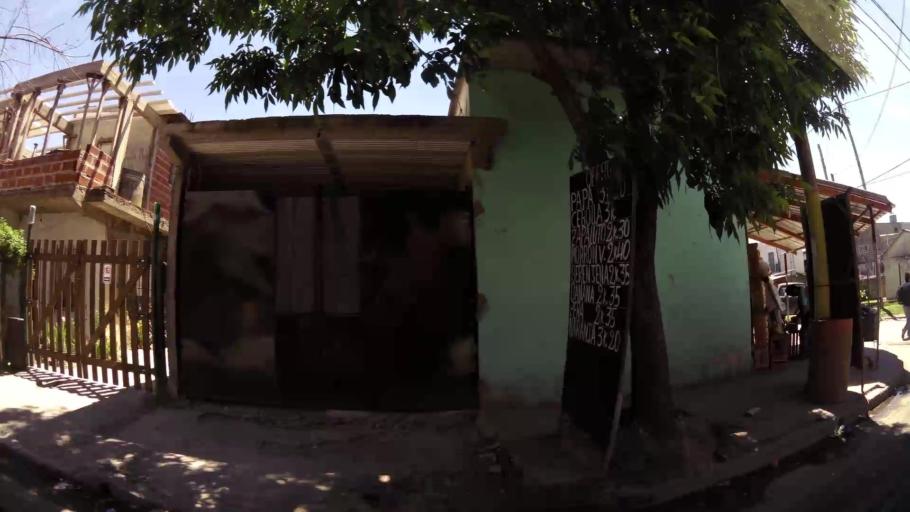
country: AR
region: Buenos Aires
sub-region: Partido de Quilmes
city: Quilmes
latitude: -34.7224
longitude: -58.3200
